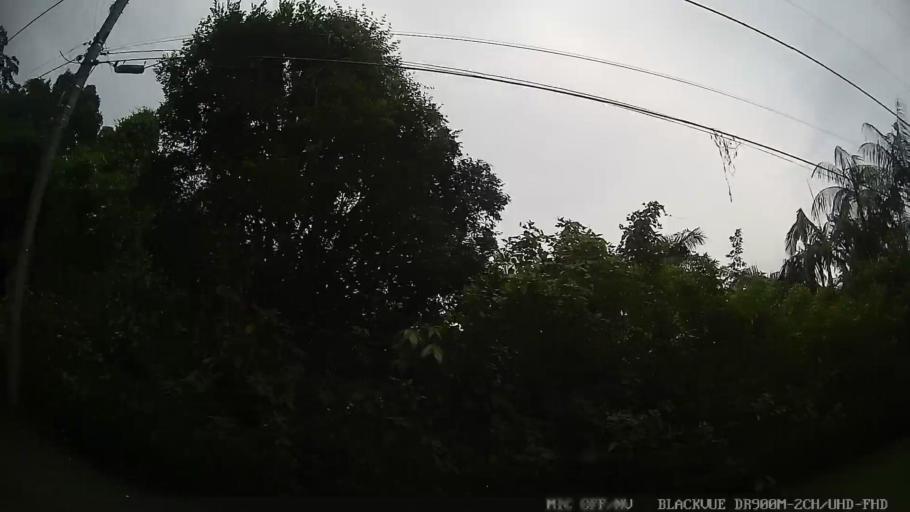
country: BR
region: Sao Paulo
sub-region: Iguape
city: Iguape
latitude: -24.6938
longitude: -47.5317
